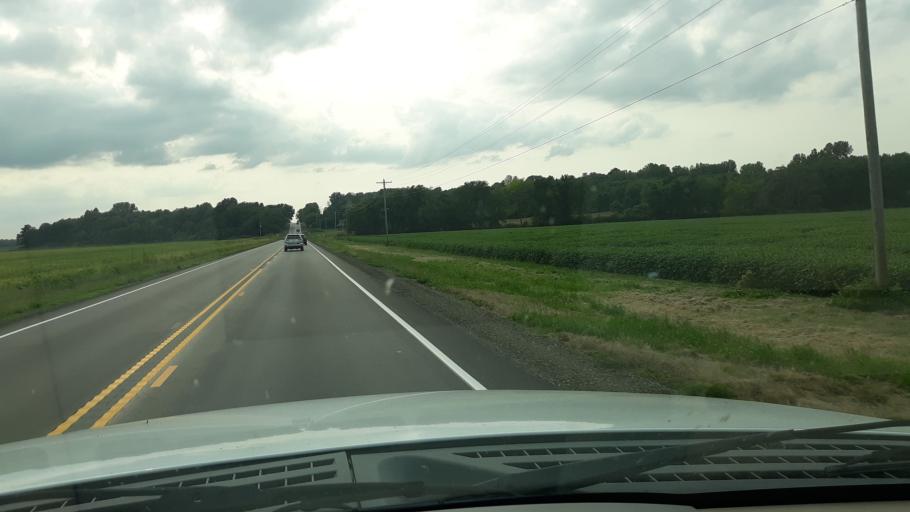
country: US
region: Indiana
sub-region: Gibson County
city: Princeton
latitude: 38.3558
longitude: -87.6468
